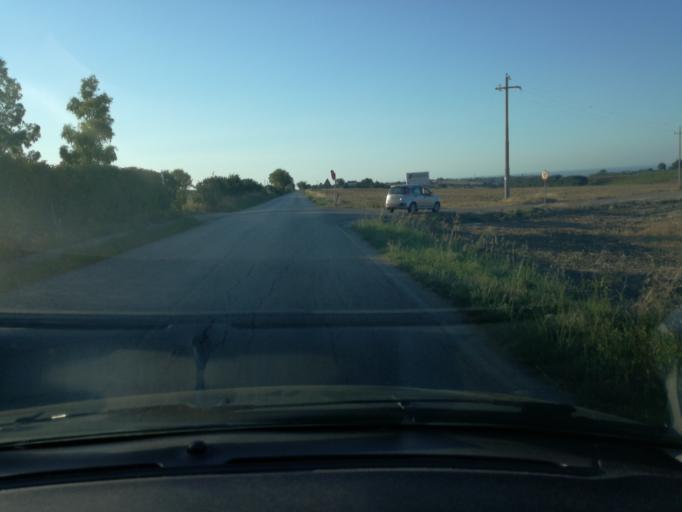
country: IT
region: Molise
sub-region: Provincia di Campobasso
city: San Giacomo degli Schiavoni
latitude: 41.9378
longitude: 14.9455
